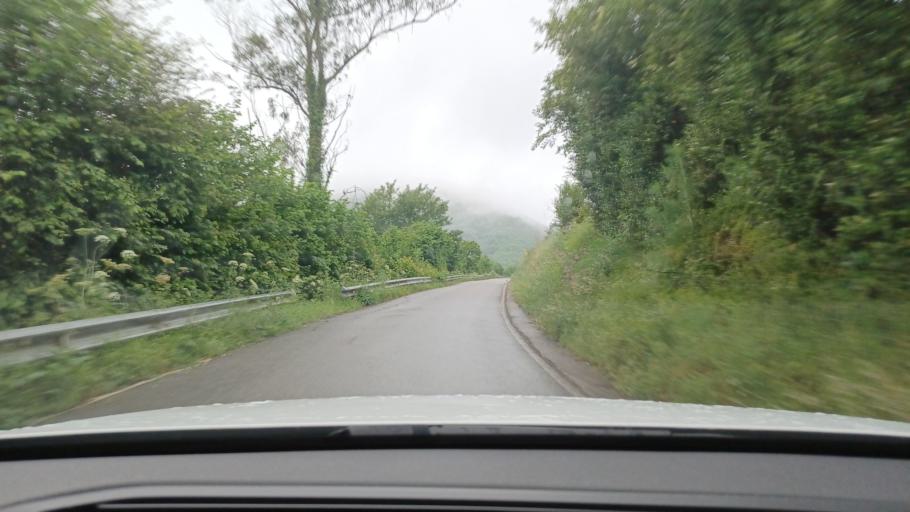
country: ES
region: Asturias
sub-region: Province of Asturias
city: Castandiello
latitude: 43.3014
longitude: -5.9370
